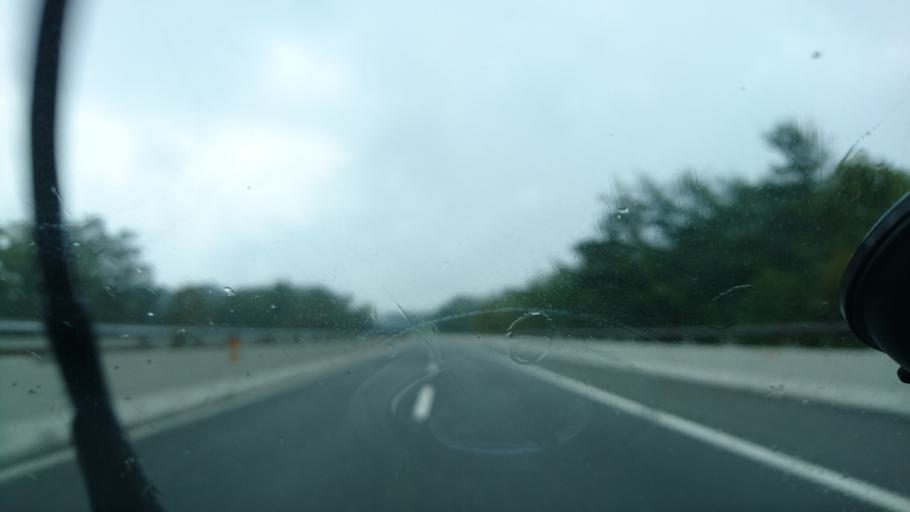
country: IT
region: Piedmont
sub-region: Provincia di Novara
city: Cressa
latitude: 45.6638
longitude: 8.5122
